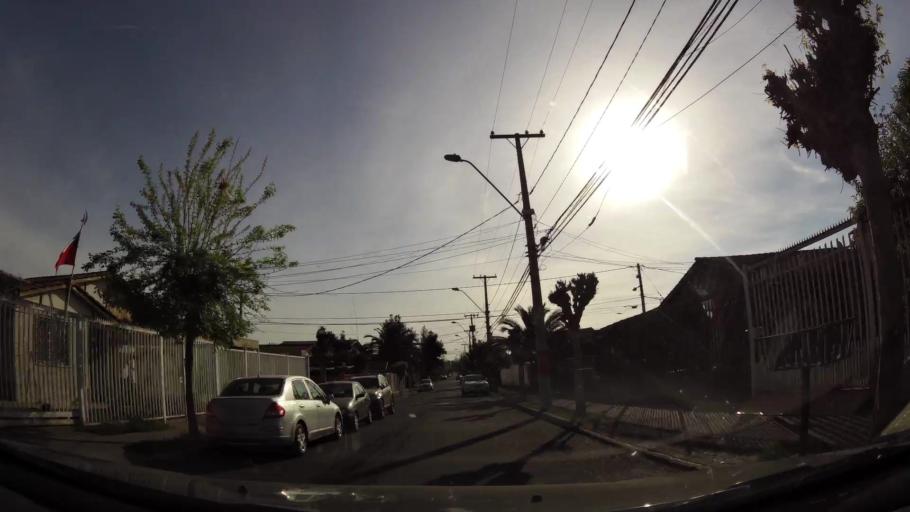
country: CL
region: Santiago Metropolitan
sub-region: Provincia de Cordillera
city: Puente Alto
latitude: -33.5778
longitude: -70.5627
